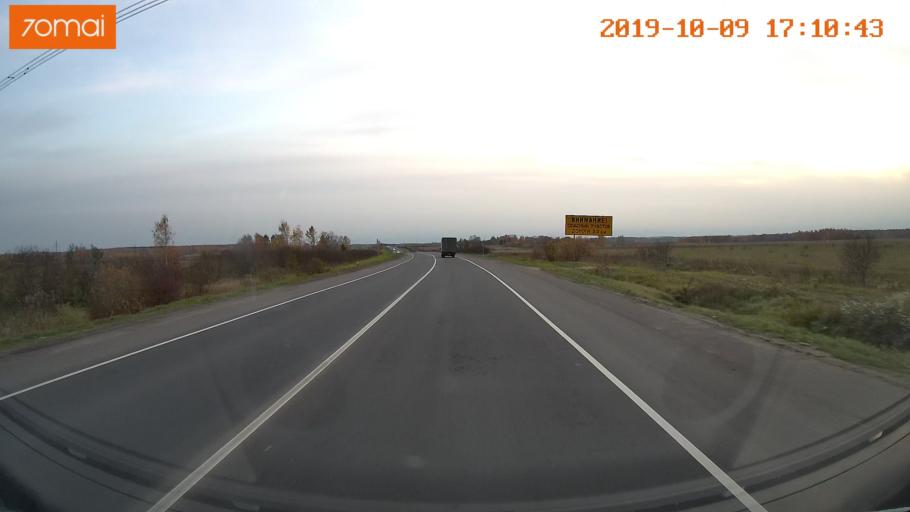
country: RU
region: Ivanovo
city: Privolzhsk
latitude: 57.3520
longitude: 41.2554
